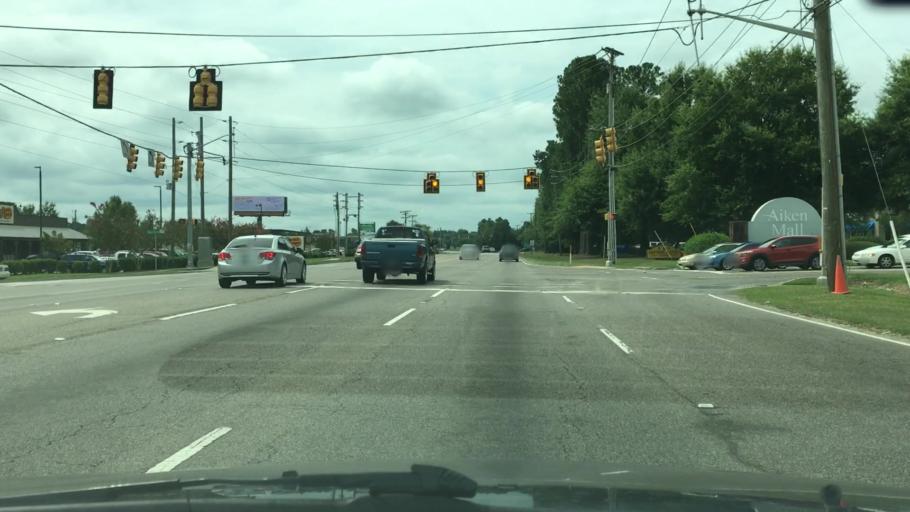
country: US
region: South Carolina
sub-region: Aiken County
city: Aiken
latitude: 33.5116
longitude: -81.7134
